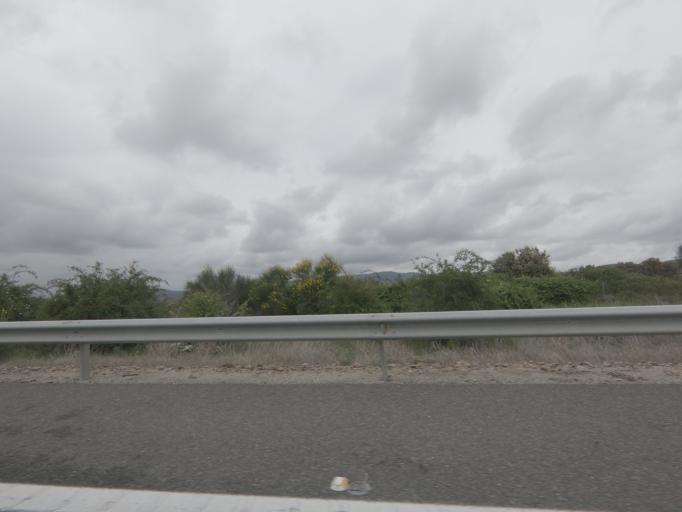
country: ES
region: Extremadura
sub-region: Provincia de Caceres
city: Aldeanueva del Camino
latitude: 40.2519
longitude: -5.9460
